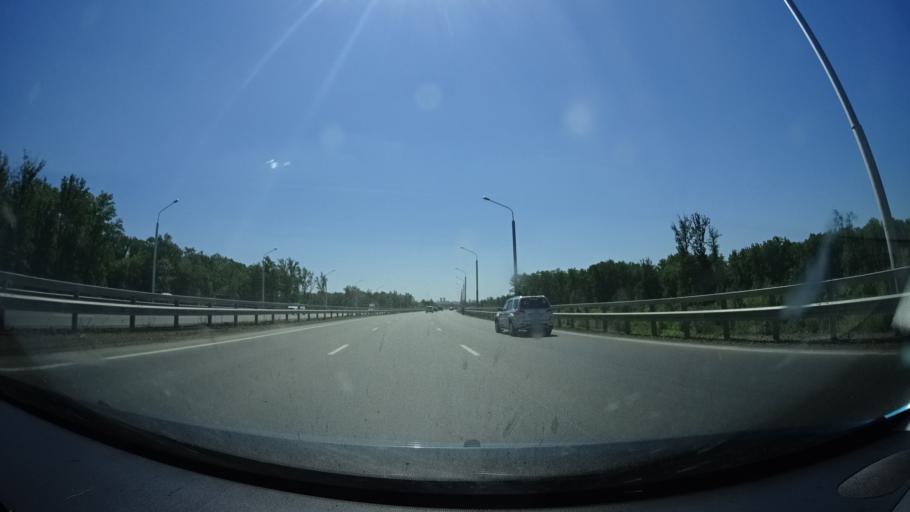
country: RU
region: Bashkortostan
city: Mikhaylovka
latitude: 54.7938
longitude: 55.9037
